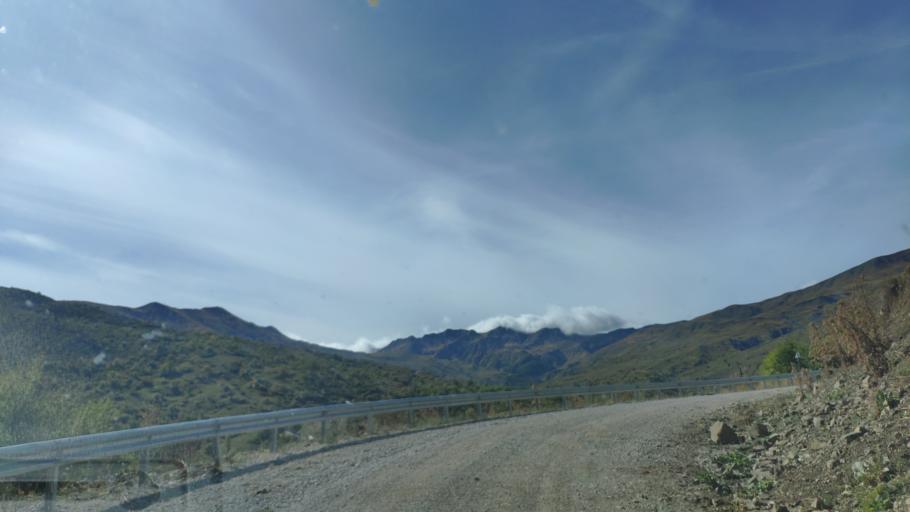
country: AL
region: Korce
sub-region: Rrethi i Devollit
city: Miras
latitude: 40.3984
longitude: 20.8429
